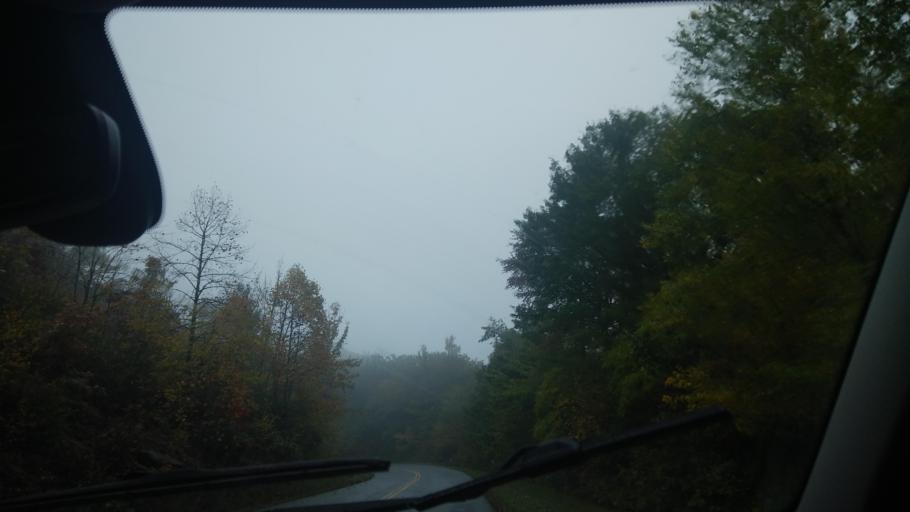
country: US
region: North Carolina
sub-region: Watauga County
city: Foscoe
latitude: 36.1226
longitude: -81.7742
